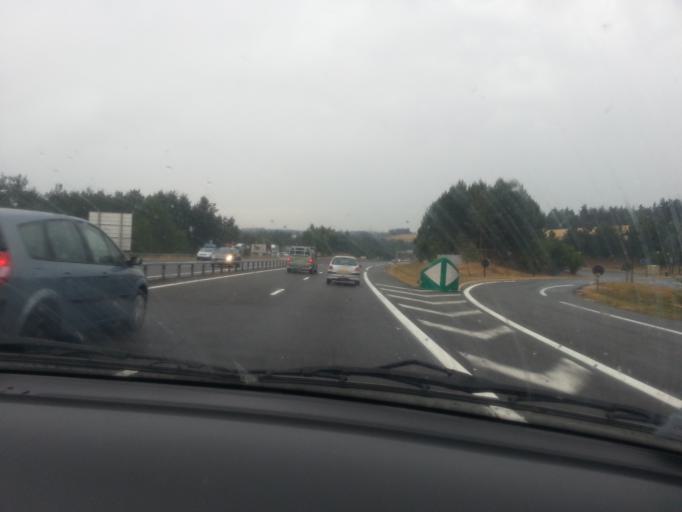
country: FR
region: Languedoc-Roussillon
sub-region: Departement de la Lozere
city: Aumont-Aubrac
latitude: 44.7431
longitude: 3.2884
